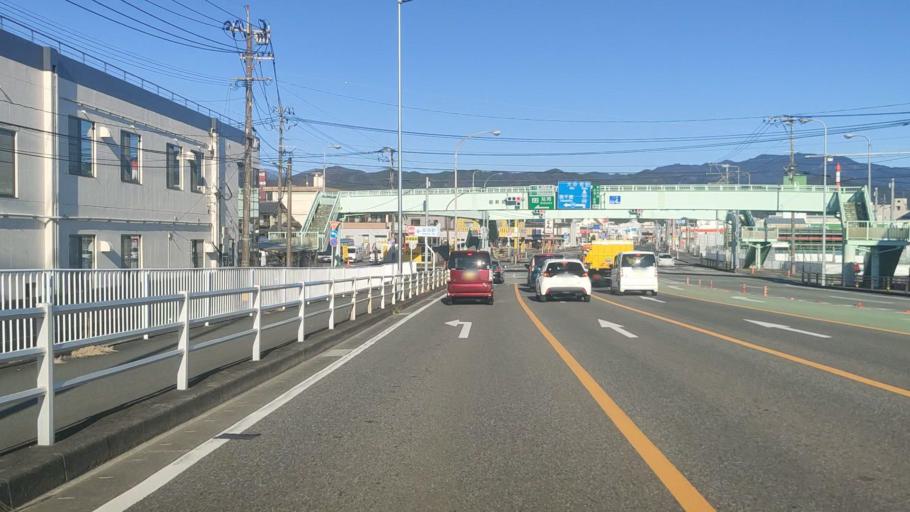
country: JP
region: Miyazaki
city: Nobeoka
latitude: 32.5860
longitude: 131.6777
